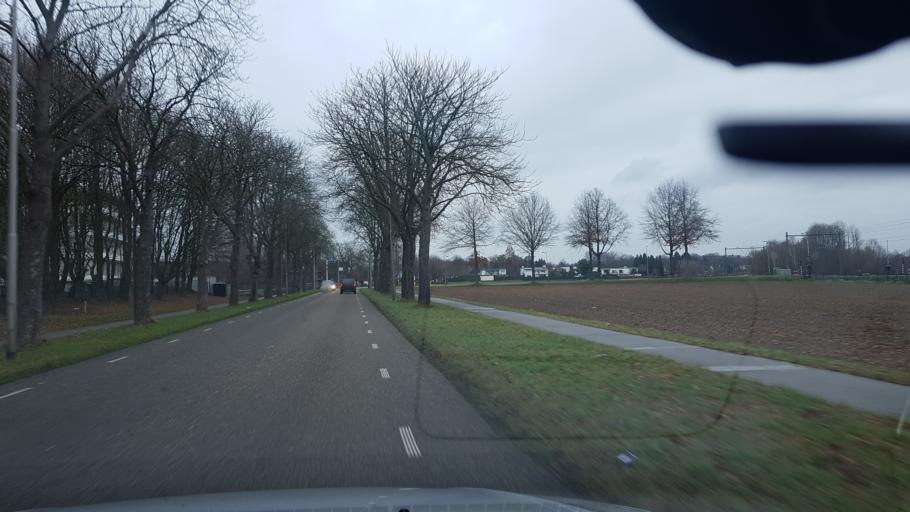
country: NL
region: Limburg
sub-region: Gemeente Schinnen
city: Puth
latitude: 50.9516
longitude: 5.8355
